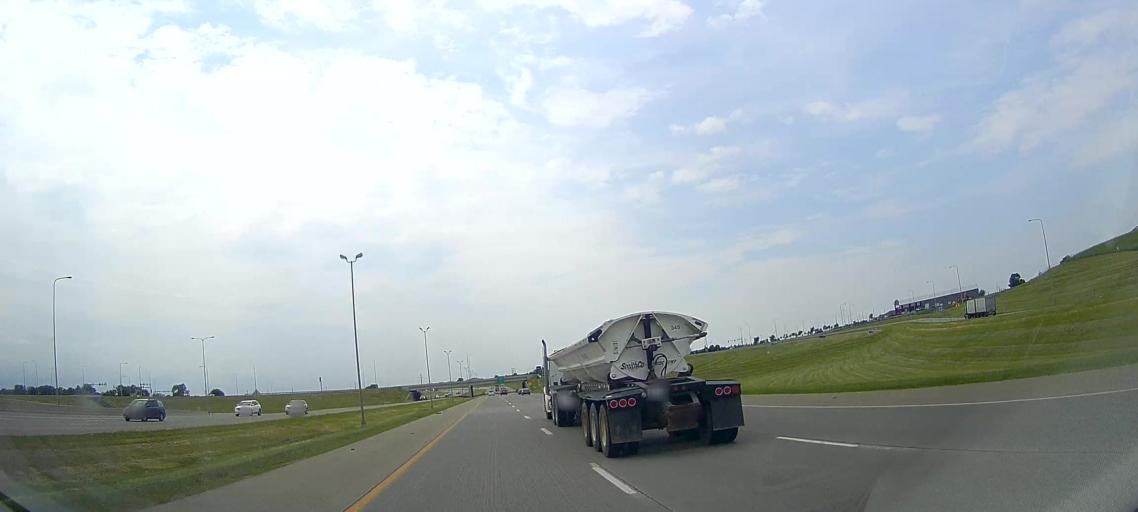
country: US
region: South Dakota
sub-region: Minnehaha County
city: Sioux Falls
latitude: 43.5753
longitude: -96.7728
